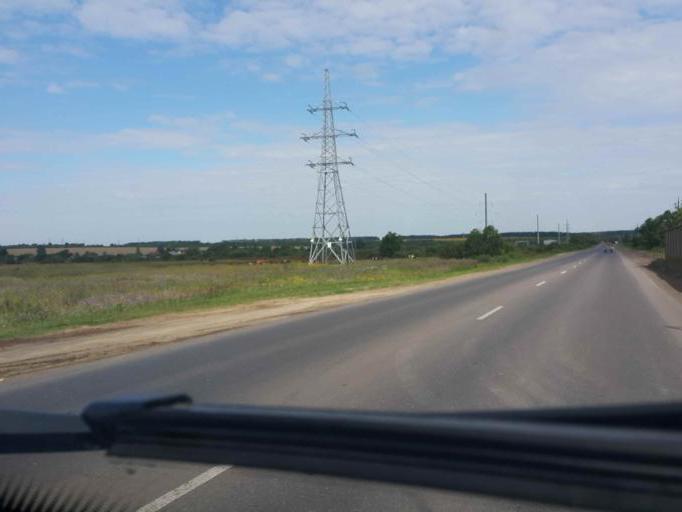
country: RU
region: Tambov
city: Bokino
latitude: 52.6426
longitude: 41.4248
